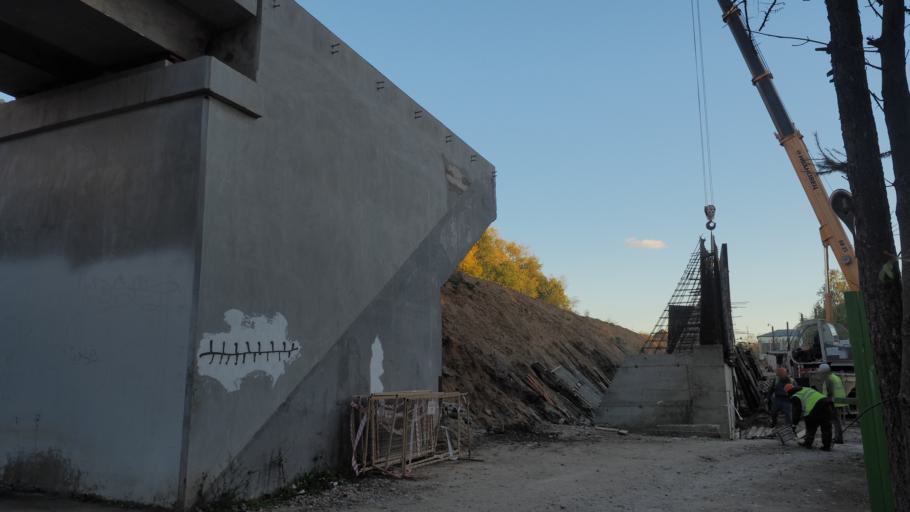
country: RU
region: Moscow
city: Pokrovskoye-Streshnevo
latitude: 55.8170
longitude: 37.4862
